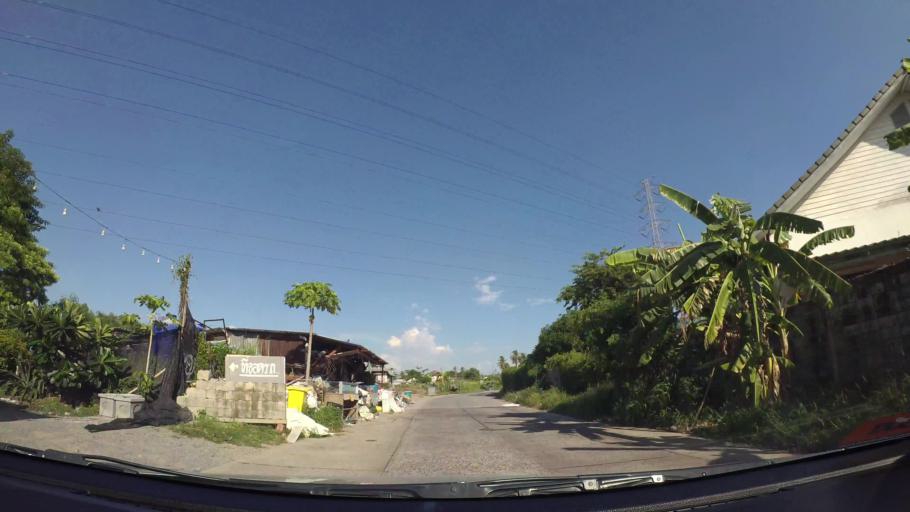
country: TH
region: Chon Buri
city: Si Racha
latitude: 13.1487
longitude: 100.9414
